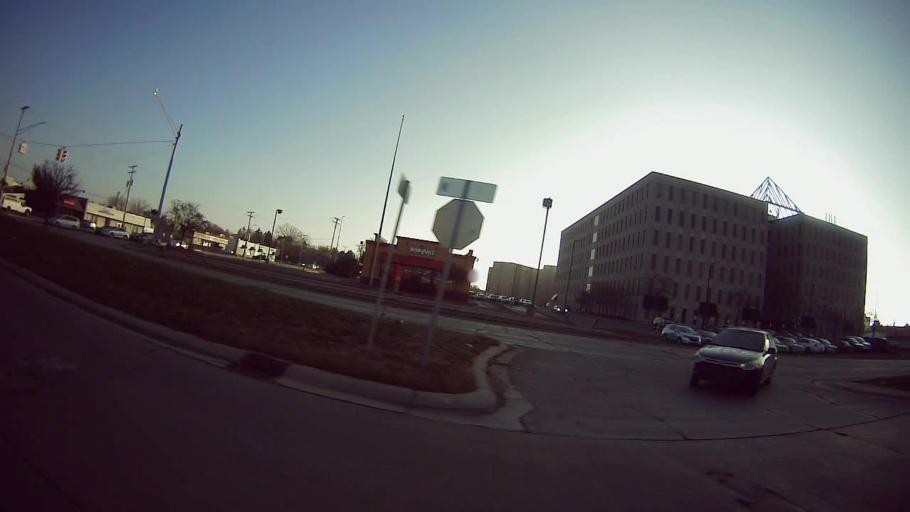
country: US
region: Michigan
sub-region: Oakland County
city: Southfield
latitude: 42.4813
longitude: -83.2023
